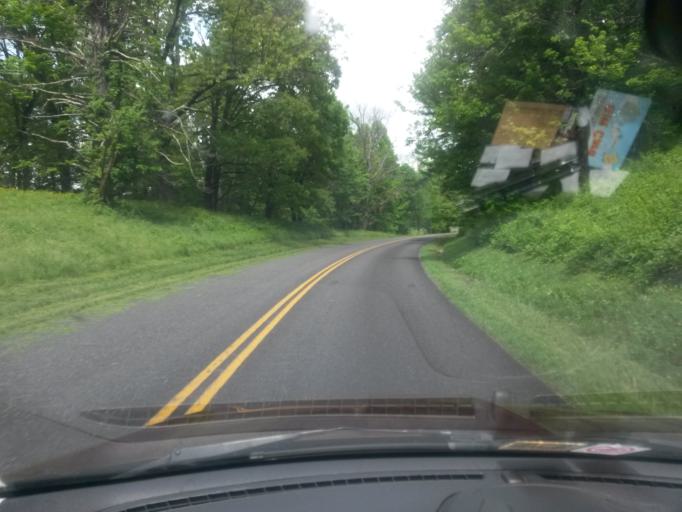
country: US
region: Virginia
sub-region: Floyd County
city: Floyd
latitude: 36.8369
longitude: -80.3258
